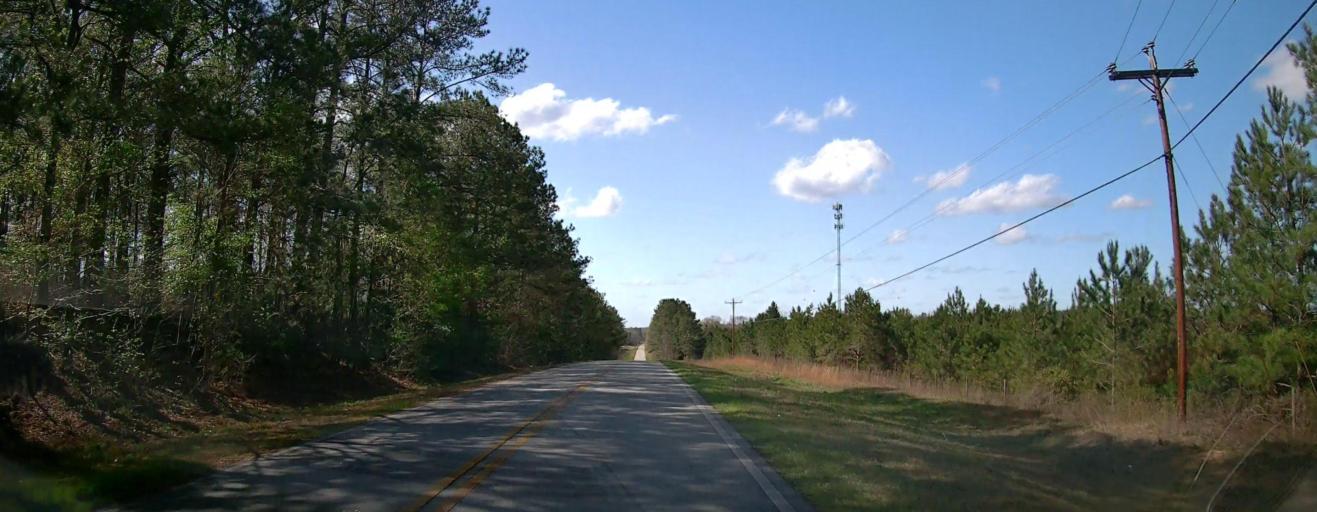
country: US
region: Georgia
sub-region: Wilkinson County
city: Gordon
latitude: 32.8365
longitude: -83.4357
